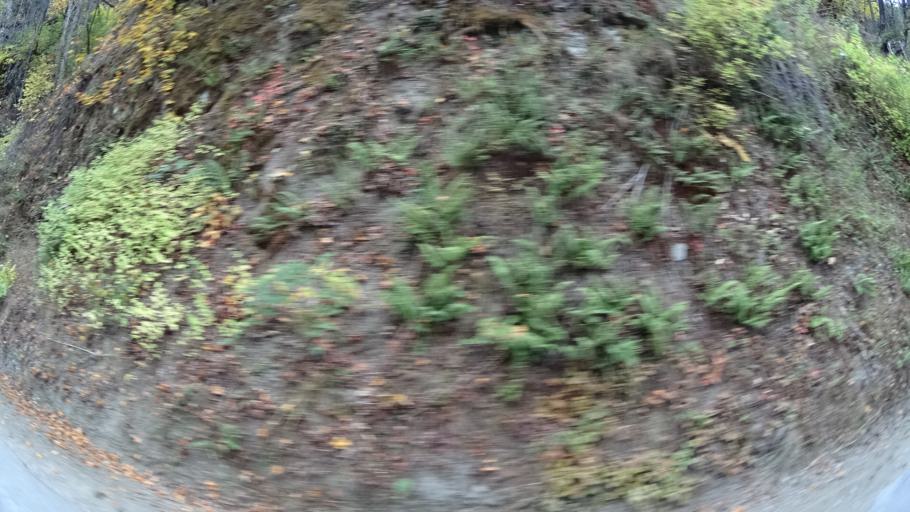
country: US
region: California
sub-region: Siskiyou County
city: Happy Camp
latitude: 41.7695
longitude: -123.3445
